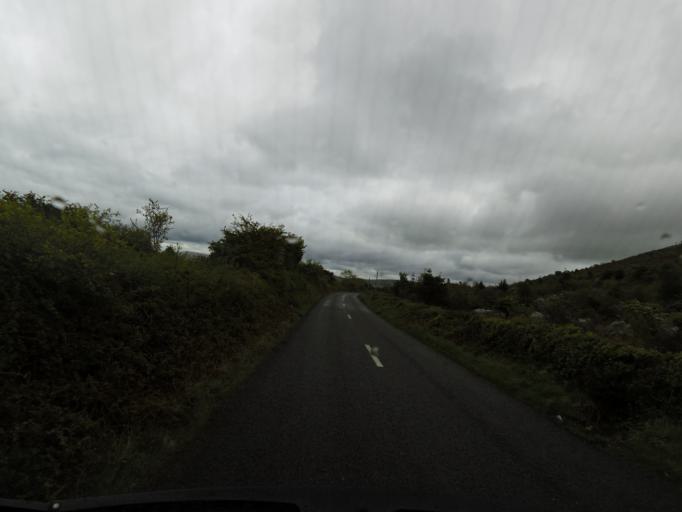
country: IE
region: Connaught
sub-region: County Galway
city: Bearna
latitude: 53.1320
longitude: -9.1903
